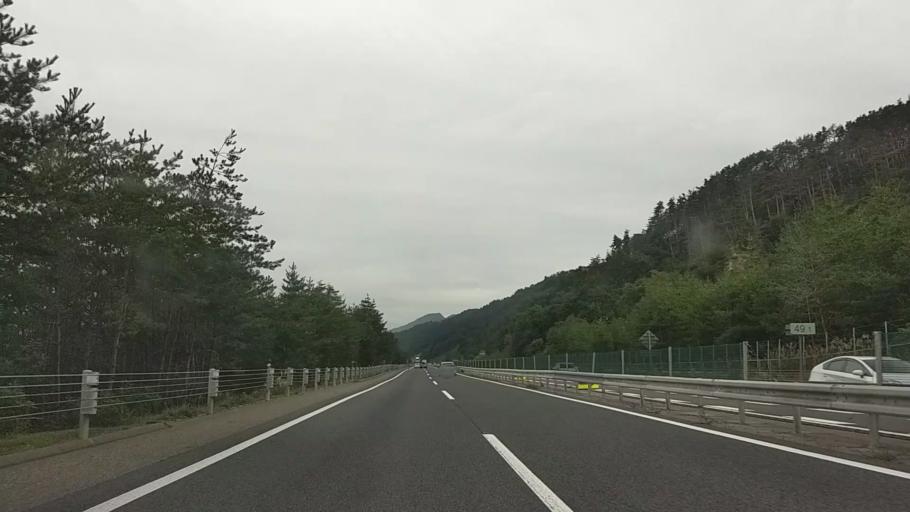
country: JP
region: Nagano
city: Hotaka
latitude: 36.4109
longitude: 138.0015
